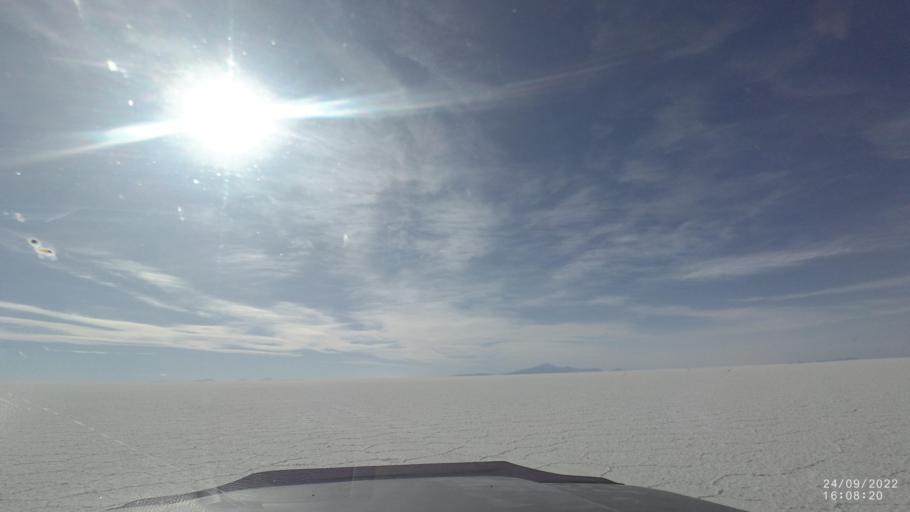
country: BO
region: Potosi
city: Colchani
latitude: -20.2936
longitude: -67.3108
